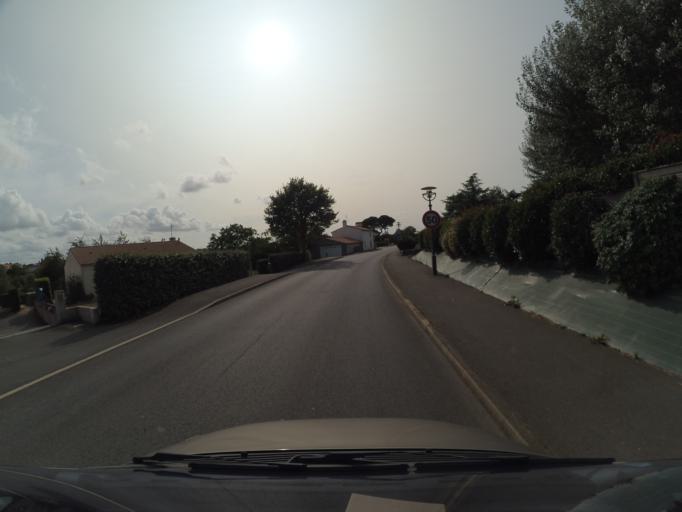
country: FR
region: Pays de la Loire
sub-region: Departement de la Vendee
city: Saint-Georges-de-Montaigu
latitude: 46.9506
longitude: -1.2948
